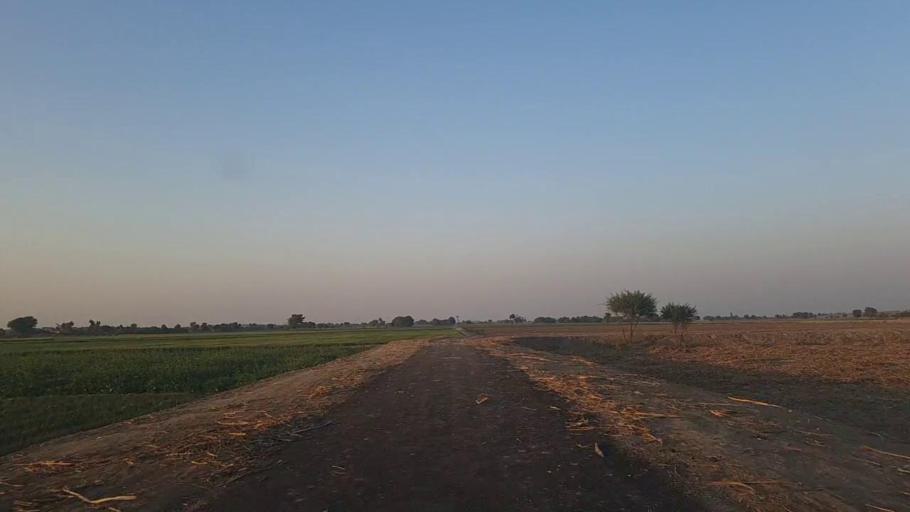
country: PK
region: Sindh
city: Jam Sahib
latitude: 26.3573
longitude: 68.7186
